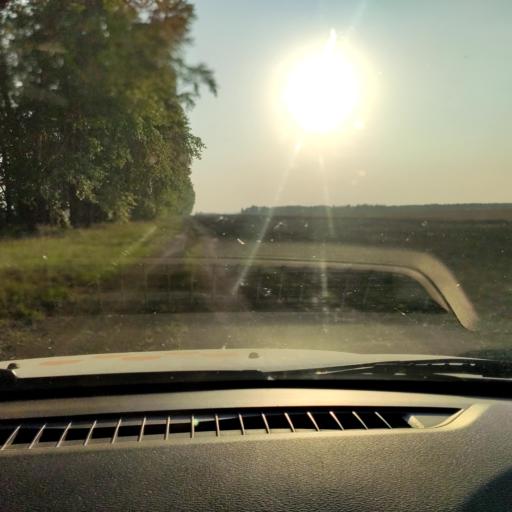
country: RU
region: Bashkortostan
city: Mikhaylovka
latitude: 54.9529
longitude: 55.8454
